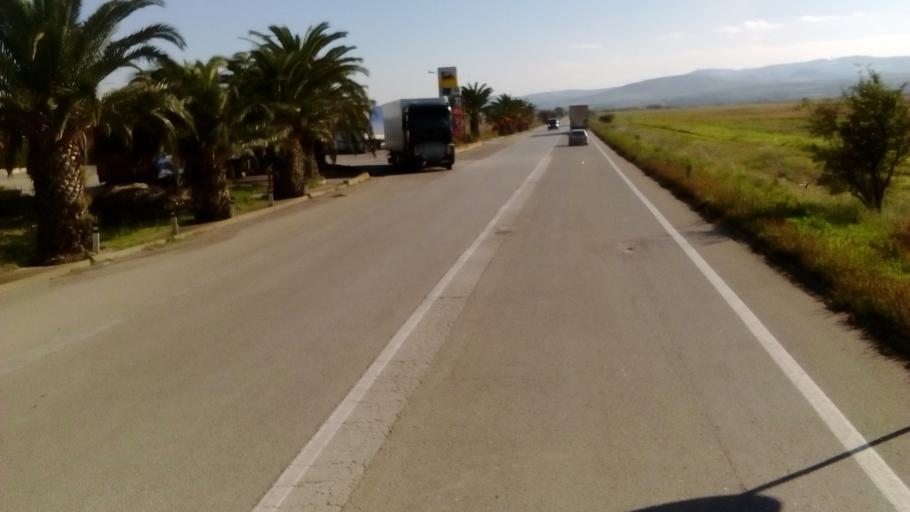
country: IT
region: Apulia
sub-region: Provincia di Foggia
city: Candela
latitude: 41.1103
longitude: 15.5854
